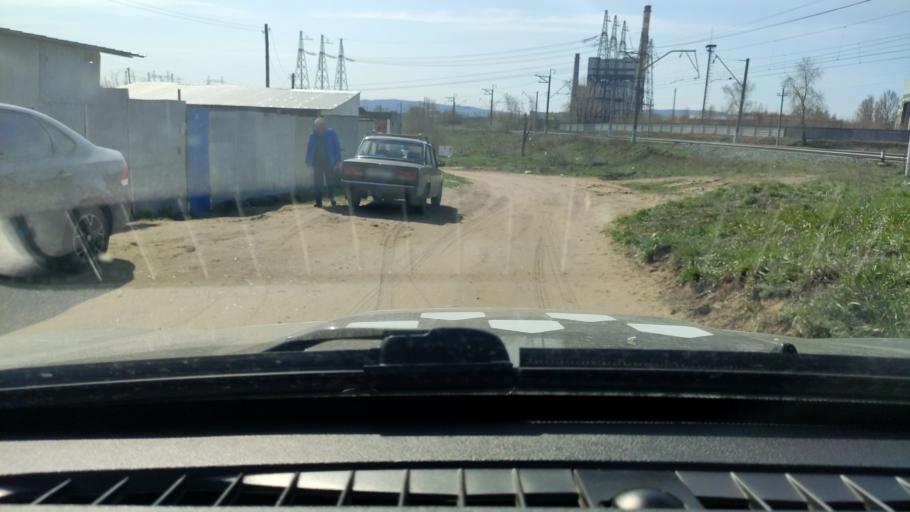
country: RU
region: Samara
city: Zhigulevsk
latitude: 53.4936
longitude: 49.4915
